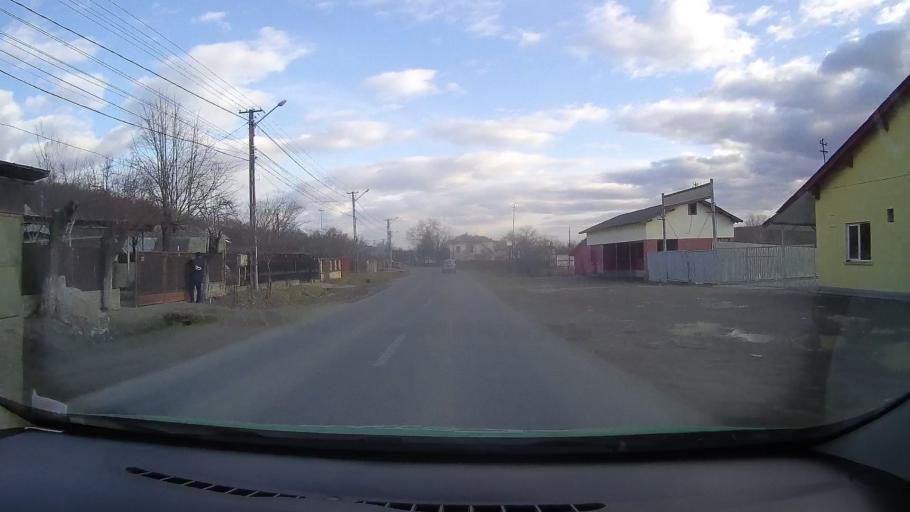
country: RO
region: Dambovita
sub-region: Comuna Gura Ocnitei
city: Gura Ocnitei
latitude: 44.9530
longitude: 25.5547
